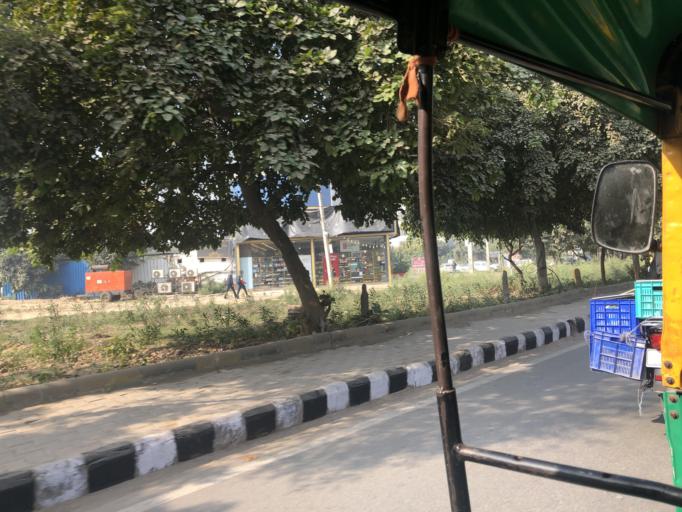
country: IN
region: Haryana
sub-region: Gurgaon
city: Gurgaon
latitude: 28.4530
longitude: 77.0751
